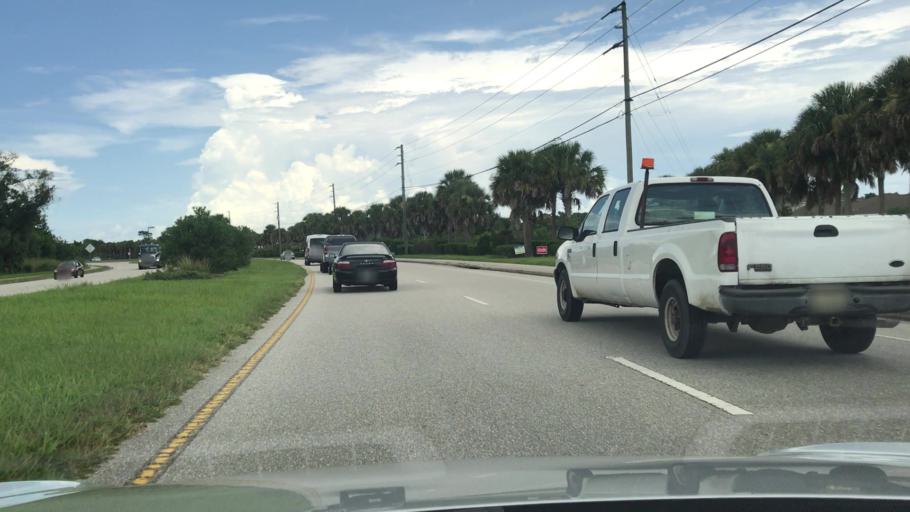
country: US
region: Florida
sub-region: Indian River County
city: Sebastian
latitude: 27.7672
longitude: -80.5094
